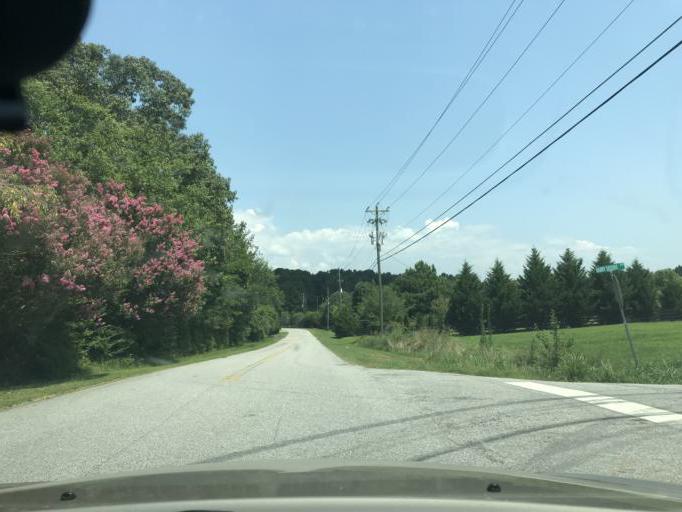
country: US
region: Georgia
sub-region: Dawson County
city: Dawsonville
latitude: 34.3382
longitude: -84.0762
